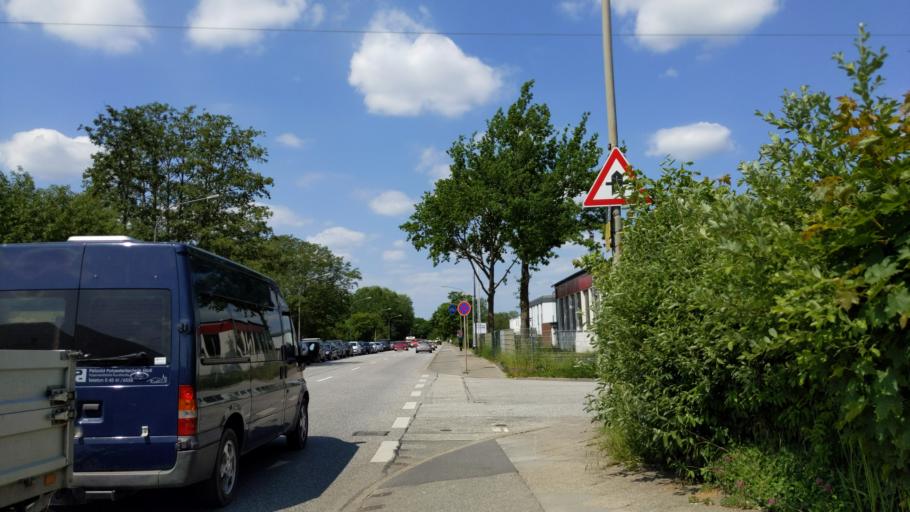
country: DE
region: Schleswig-Holstein
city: Luebeck
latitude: 53.8388
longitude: 10.6652
